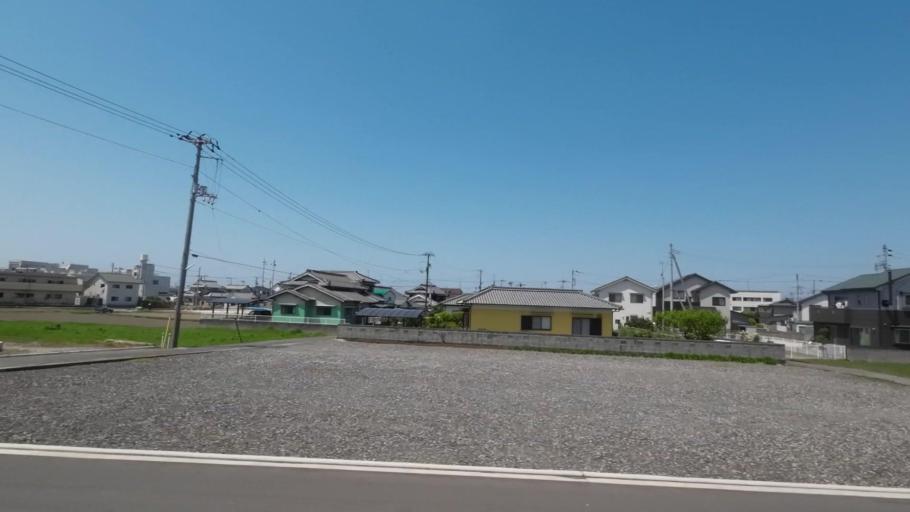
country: JP
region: Ehime
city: Hojo
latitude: 33.9484
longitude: 132.7715
